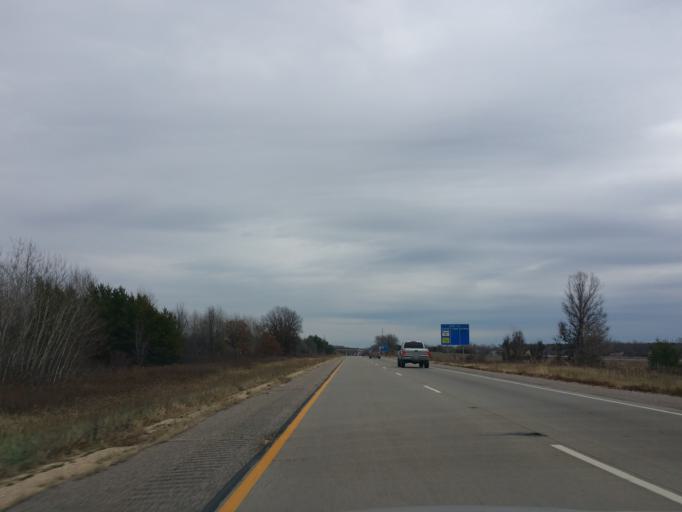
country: US
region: Wisconsin
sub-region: Juneau County
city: New Lisbon
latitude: 43.8965
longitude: -90.1803
